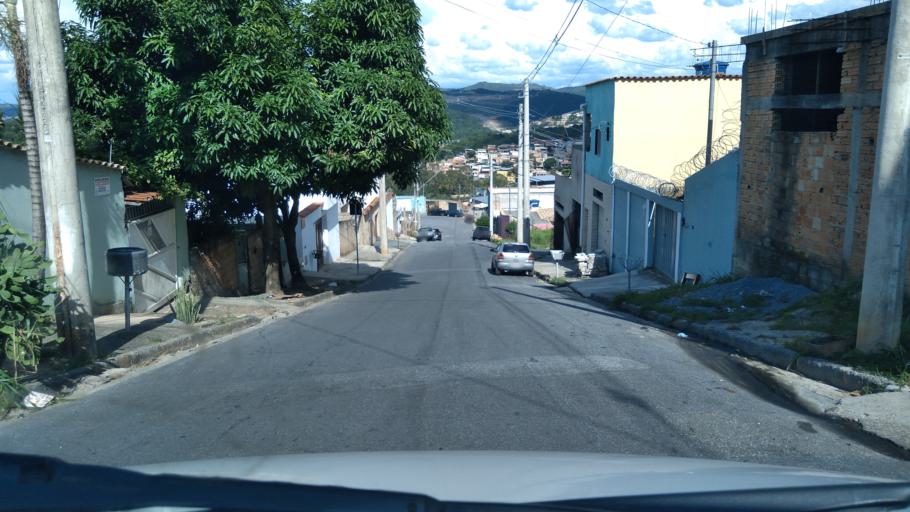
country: BR
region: Minas Gerais
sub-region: Belo Horizonte
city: Belo Horizonte
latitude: -19.8566
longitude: -43.8804
